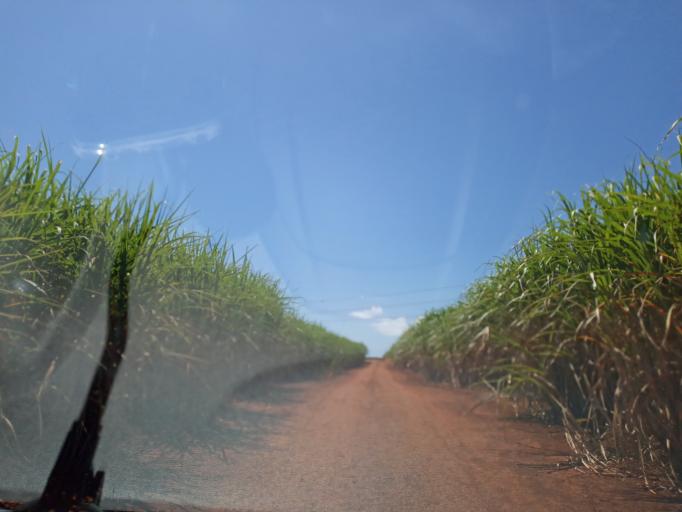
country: BR
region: Goias
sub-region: Itumbiara
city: Itumbiara
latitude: -18.4408
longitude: -49.1379
